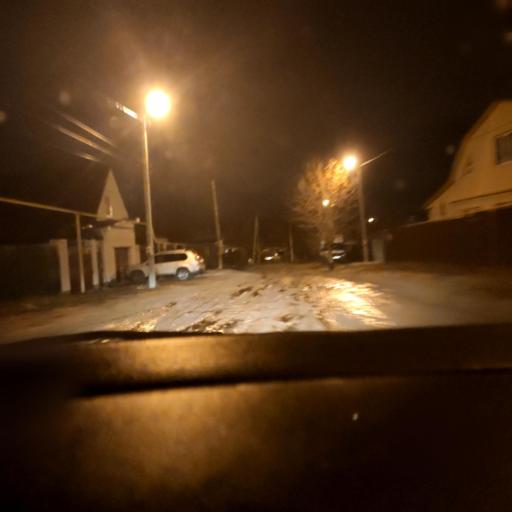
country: RU
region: Voronezj
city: Podgornoye
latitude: 51.7303
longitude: 39.1481
